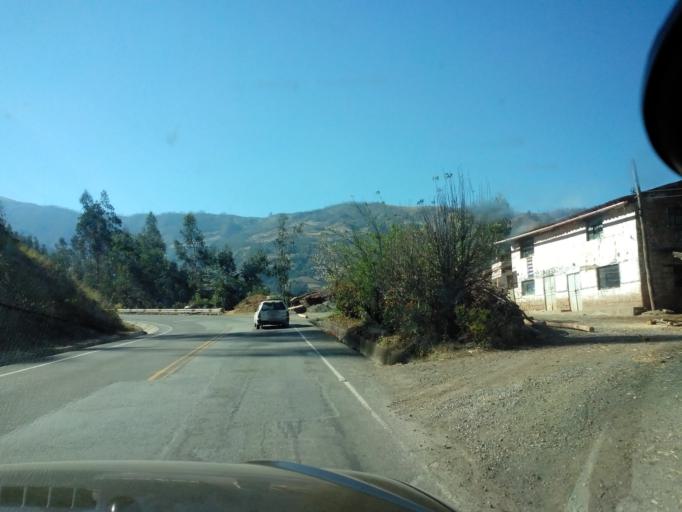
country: PE
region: Apurimac
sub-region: Provincia de Abancay
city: Tamburco
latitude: -13.6185
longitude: -72.8578
